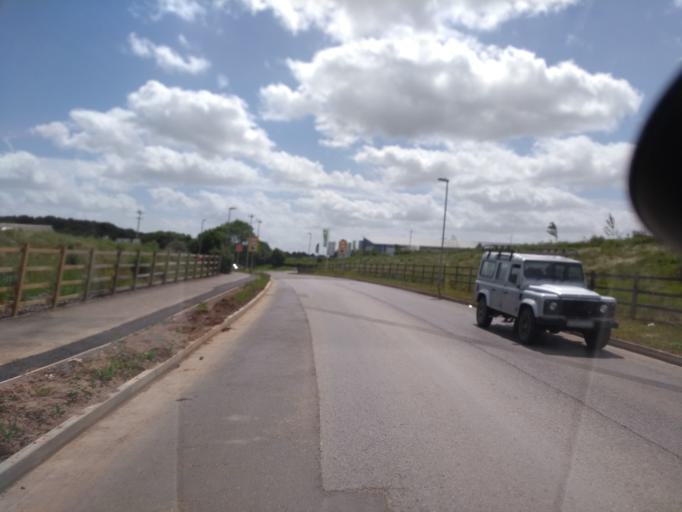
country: GB
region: England
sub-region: Somerset
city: North Petherton
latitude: 51.1048
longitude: -2.9997
